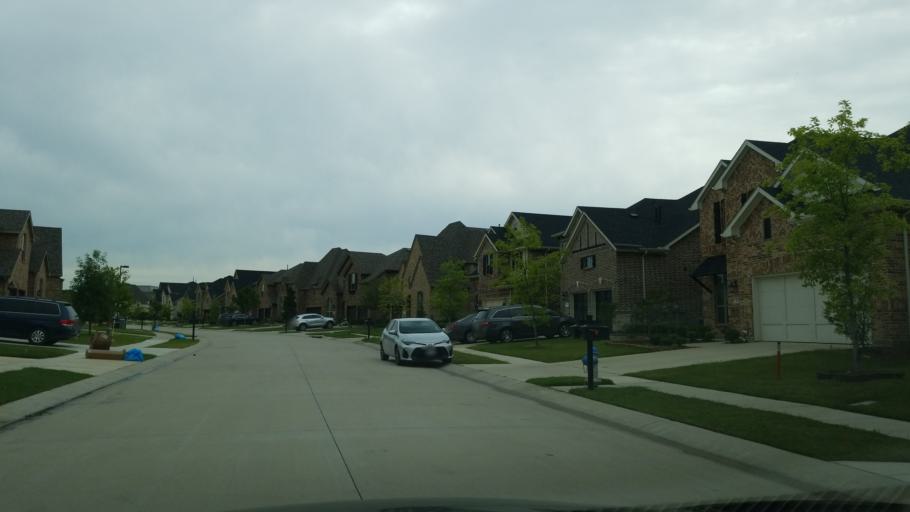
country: US
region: Texas
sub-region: Dallas County
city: Coppell
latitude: 32.9009
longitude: -96.9892
